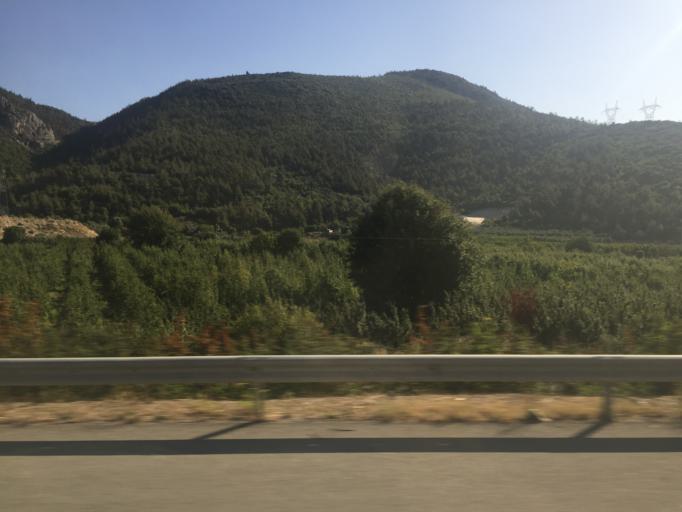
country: TR
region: Bursa
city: Kestel
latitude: 40.2381
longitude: 29.2635
